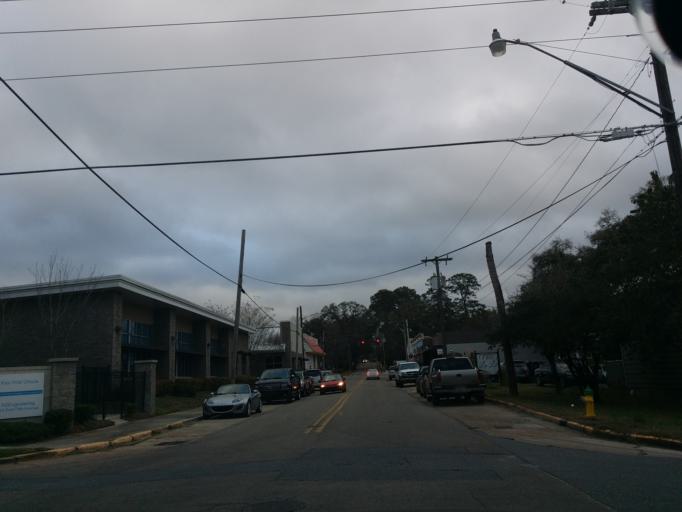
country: US
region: Florida
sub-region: Leon County
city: Tallahassee
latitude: 30.4547
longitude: -84.2819
